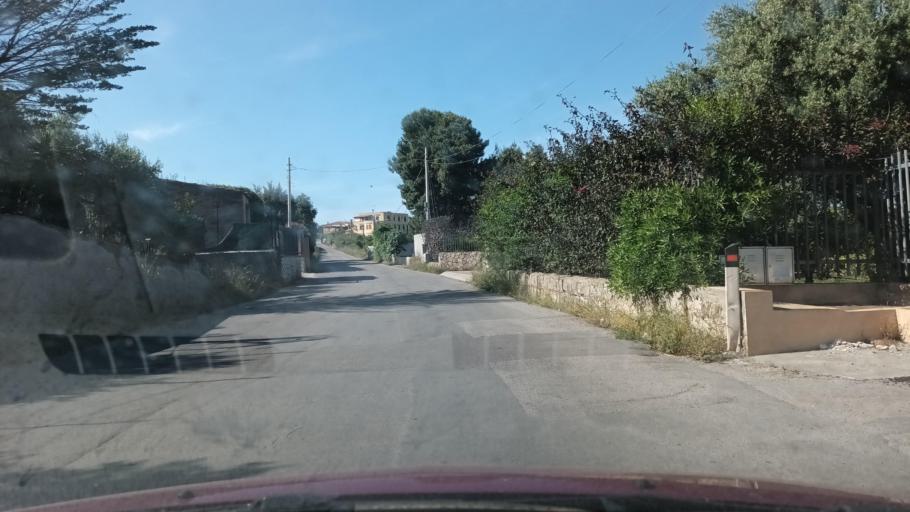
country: IT
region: Sicily
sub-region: Palermo
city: Bagheria
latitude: 38.0646
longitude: 13.5188
